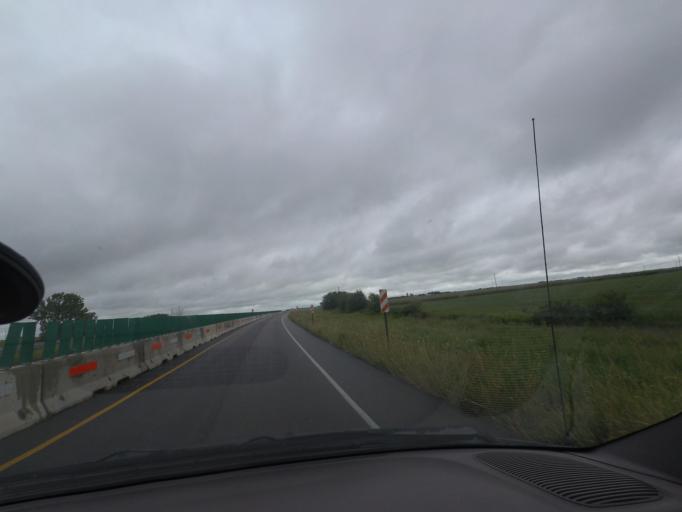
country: US
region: Illinois
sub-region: Piatt County
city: Cerro Gordo
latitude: 40.0142
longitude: -88.7666
